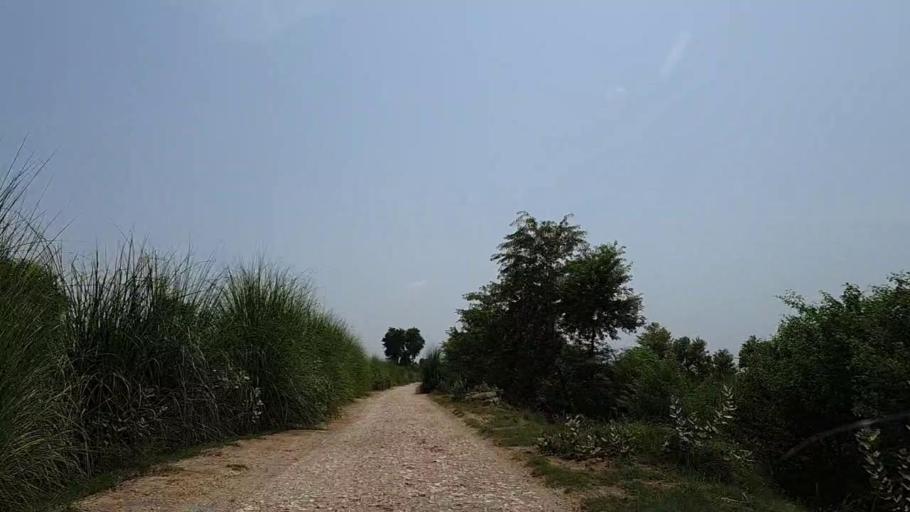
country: PK
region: Sindh
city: Adilpur
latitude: 27.9387
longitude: 69.3955
